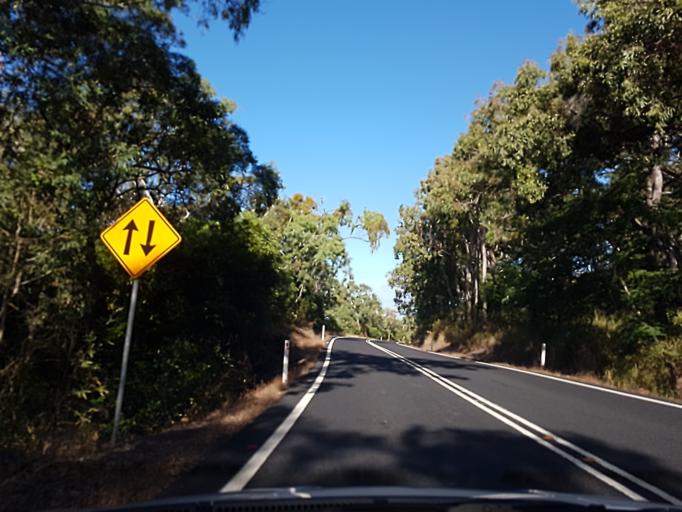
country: AU
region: Queensland
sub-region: Cairns
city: Palm Cove
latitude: -16.7070
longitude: 145.6292
